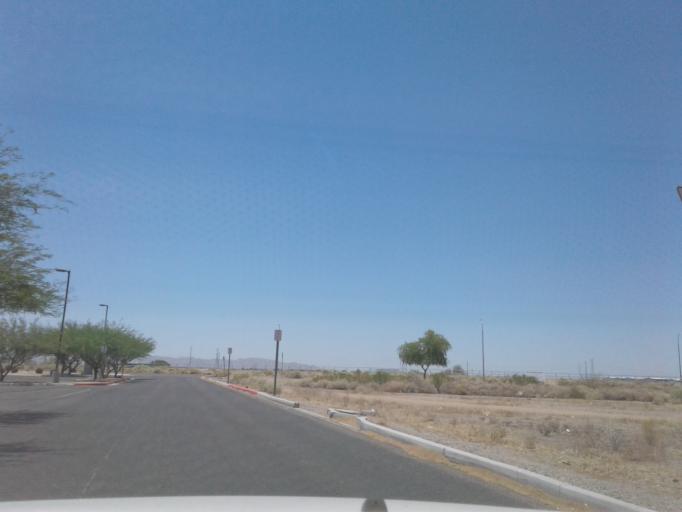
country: US
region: Arizona
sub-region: Maricopa County
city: Litchfield Park
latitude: 33.5161
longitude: -112.2951
